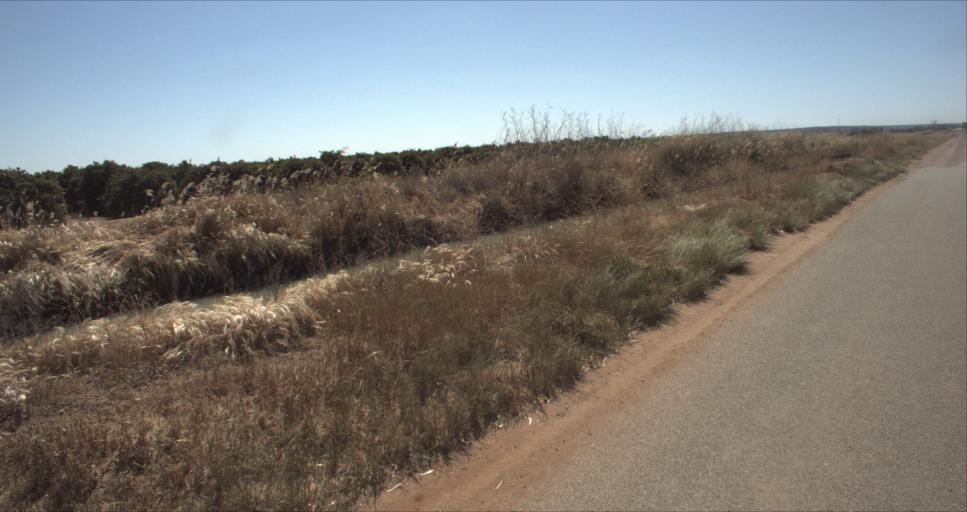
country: AU
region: New South Wales
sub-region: Leeton
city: Leeton
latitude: -34.4933
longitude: 146.4218
